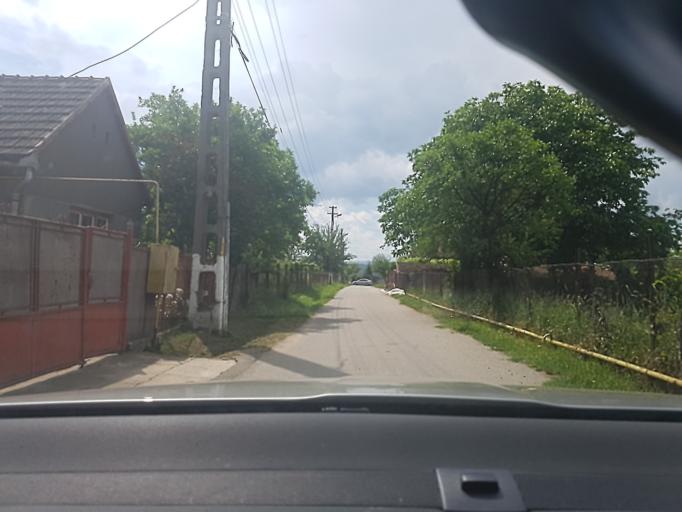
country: RO
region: Hunedoara
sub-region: Comuna Calan
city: Calan
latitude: 45.7196
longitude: 23.0174
